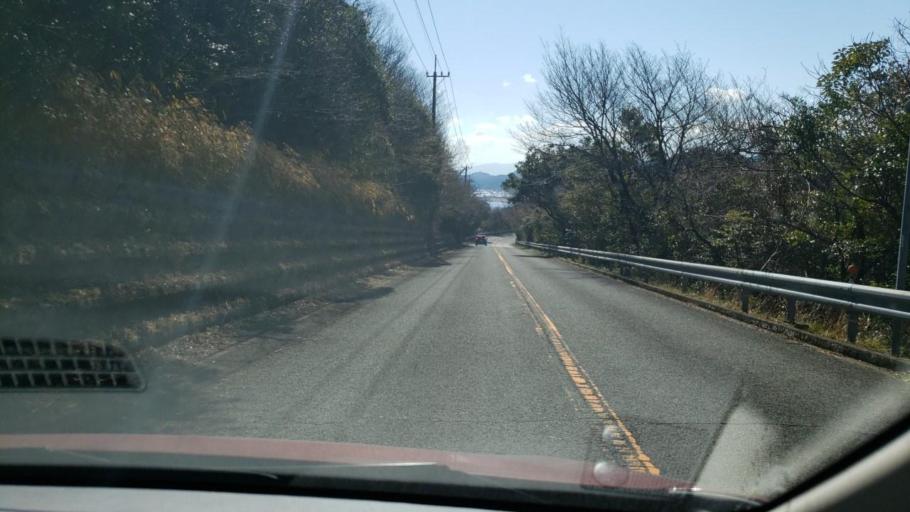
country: JP
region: Tokushima
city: Narutocho-mitsuishi
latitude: 34.2364
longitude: 134.6056
